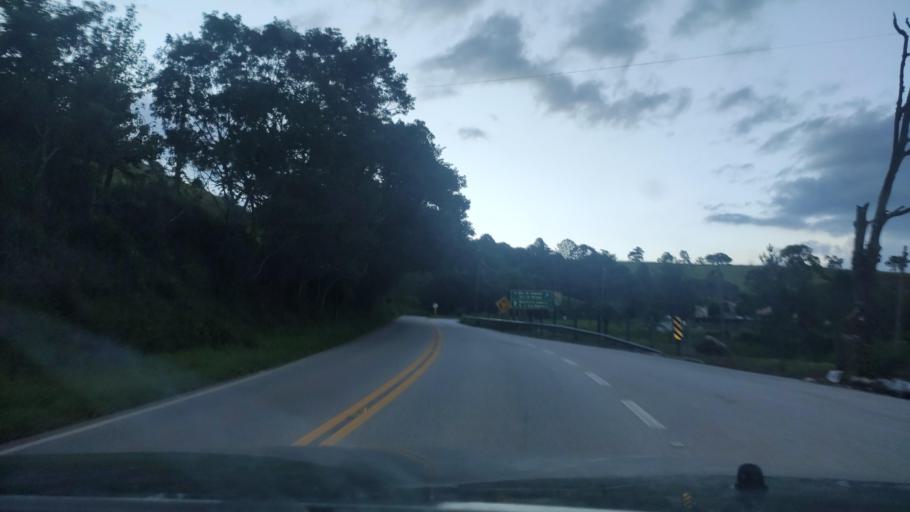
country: BR
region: Sao Paulo
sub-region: Campos Do Jordao
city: Campos do Jordao
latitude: -22.8173
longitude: -45.7510
